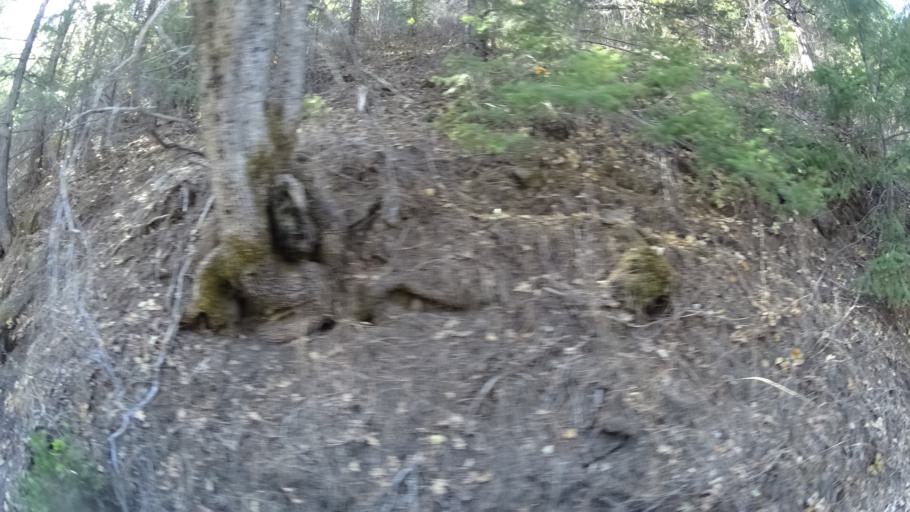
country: US
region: California
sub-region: Siskiyou County
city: Yreka
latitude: 41.8554
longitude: -122.7732
